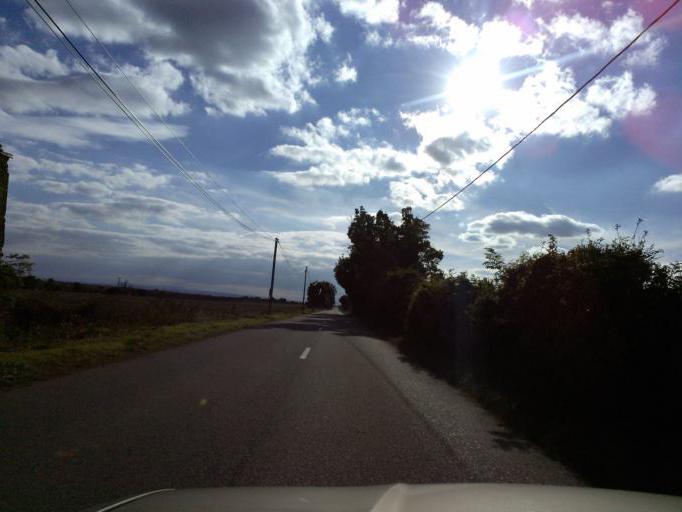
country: FR
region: Provence-Alpes-Cote d'Azur
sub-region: Departement des Alpes-de-Haute-Provence
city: Valensole
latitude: 43.8586
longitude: 6.0019
